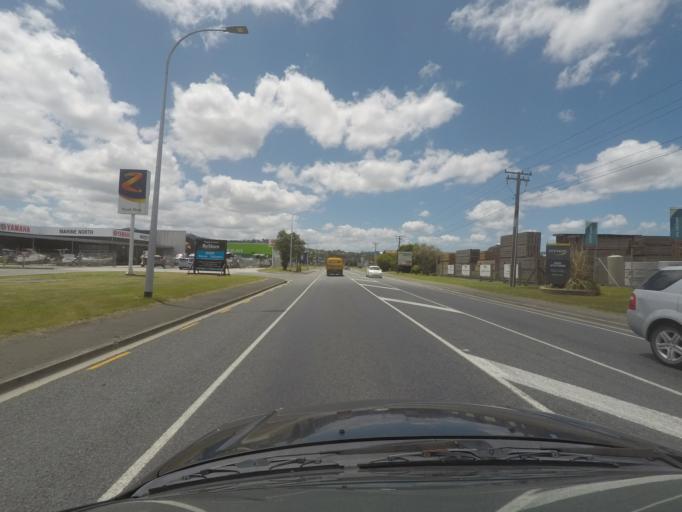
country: NZ
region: Northland
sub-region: Whangarei
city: Whangarei
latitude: -35.7418
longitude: 174.3320
